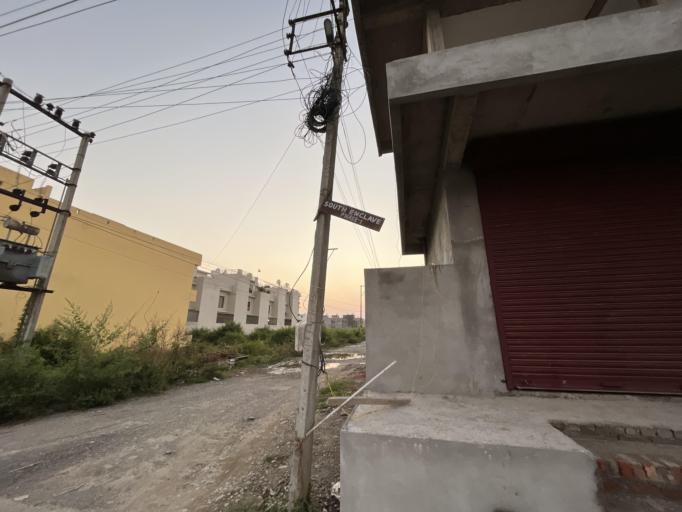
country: IN
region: Uttarakhand
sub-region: Naini Tal
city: Haldwani
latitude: 29.2024
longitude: 79.5006
